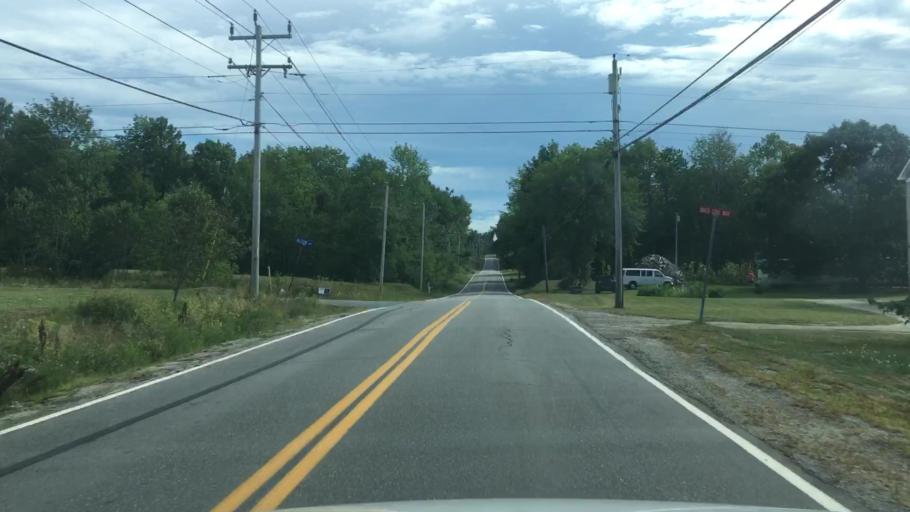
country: US
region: Maine
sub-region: Hancock County
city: Ellsworth
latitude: 44.4939
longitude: -68.4202
